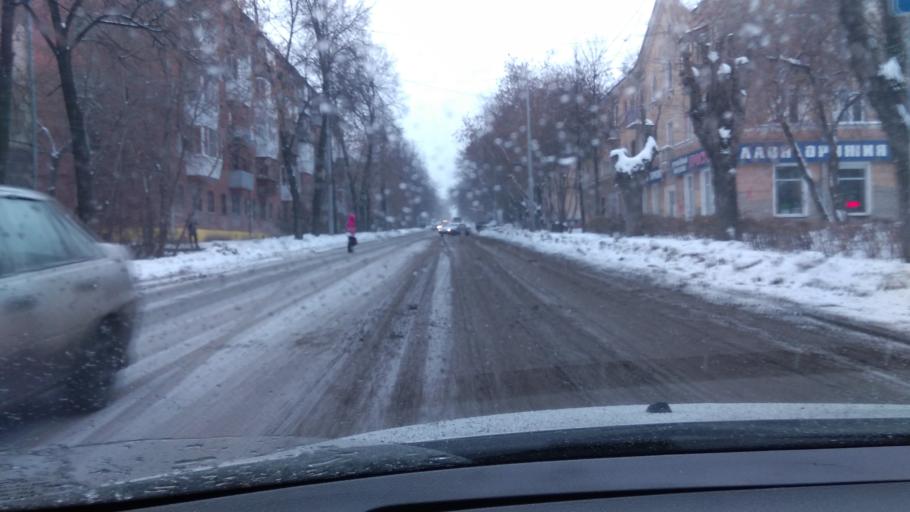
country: RU
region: Sverdlovsk
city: Yekaterinburg
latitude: 56.8943
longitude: 60.5864
